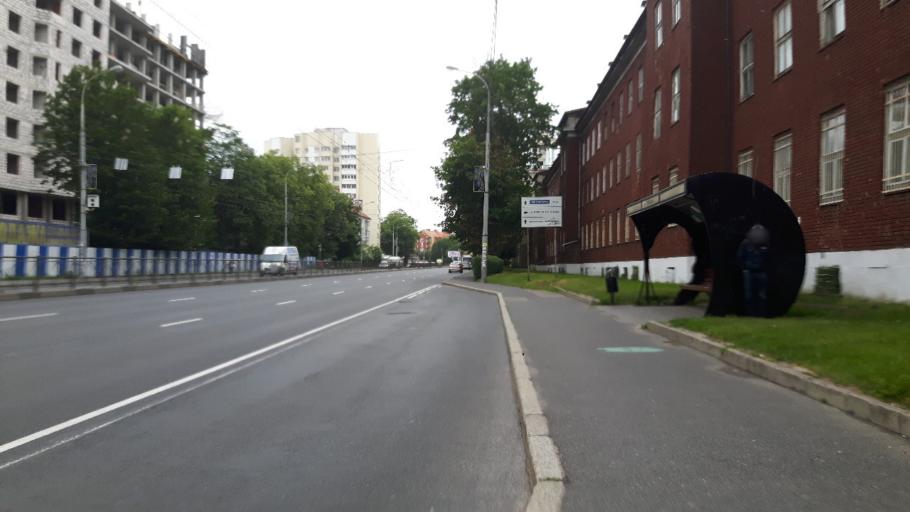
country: RU
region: Kaliningrad
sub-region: Gorod Kaliningrad
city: Kaliningrad
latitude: 54.7339
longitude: 20.4848
